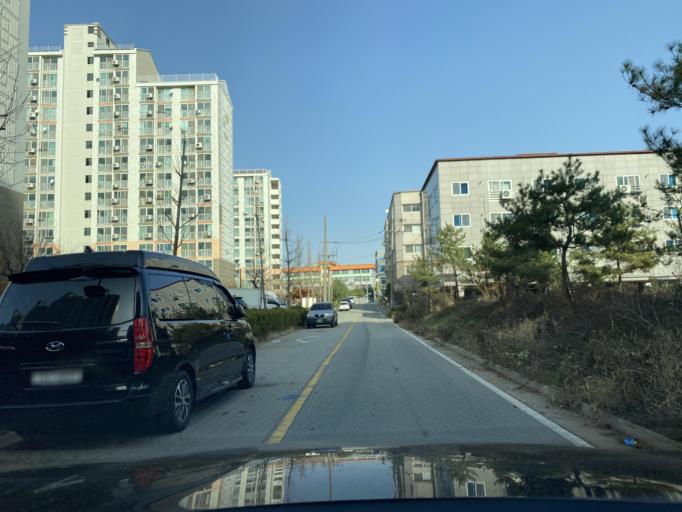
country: KR
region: Chungcheongnam-do
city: Yesan
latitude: 36.6964
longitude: 126.8352
